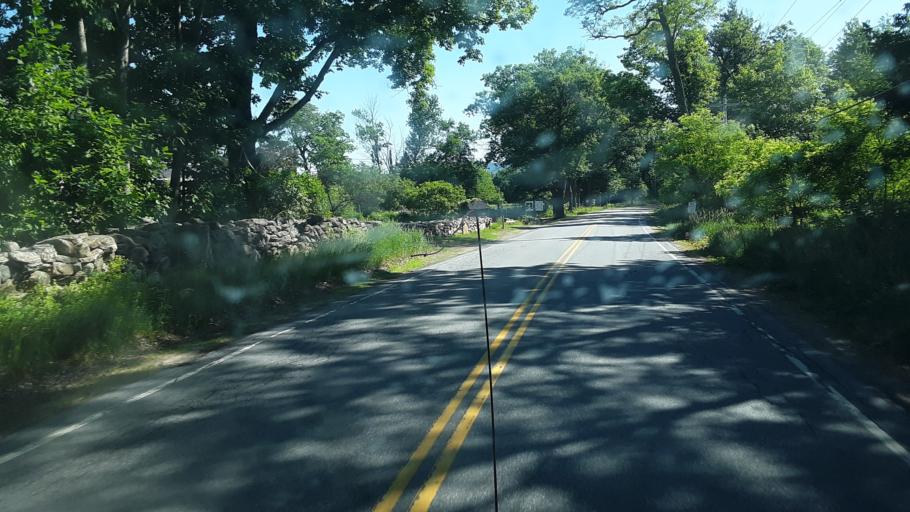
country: US
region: New Hampshire
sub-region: Grafton County
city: North Haverhill
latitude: 44.0853
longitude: -71.9650
